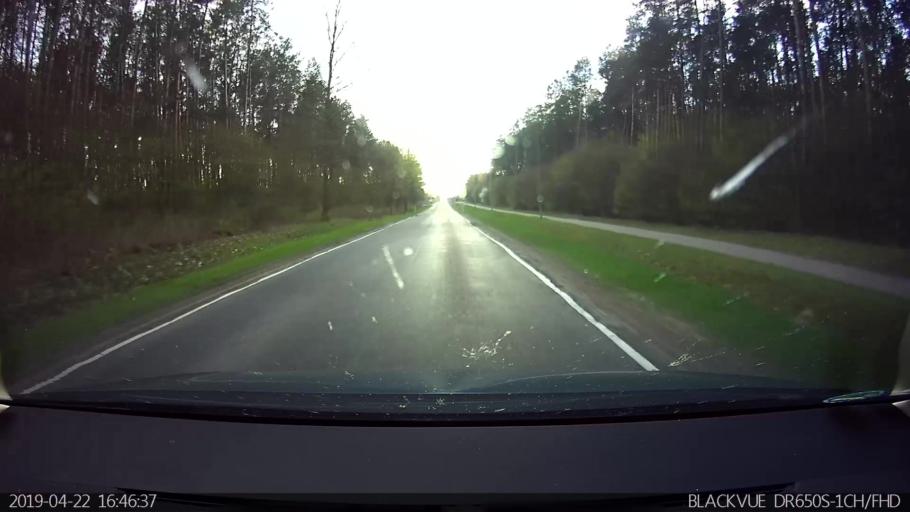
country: PL
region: Podlasie
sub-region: Powiat siemiatycki
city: Siemiatycze
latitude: 52.4351
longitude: 22.8982
